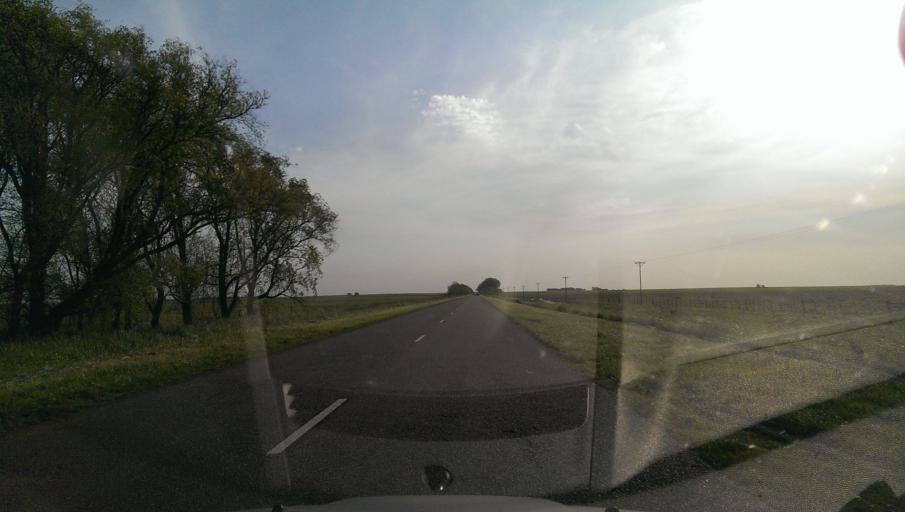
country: AR
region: Buenos Aires
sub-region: Partido de General La Madrid
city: General La Madrid
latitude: -37.5725
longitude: -61.3340
